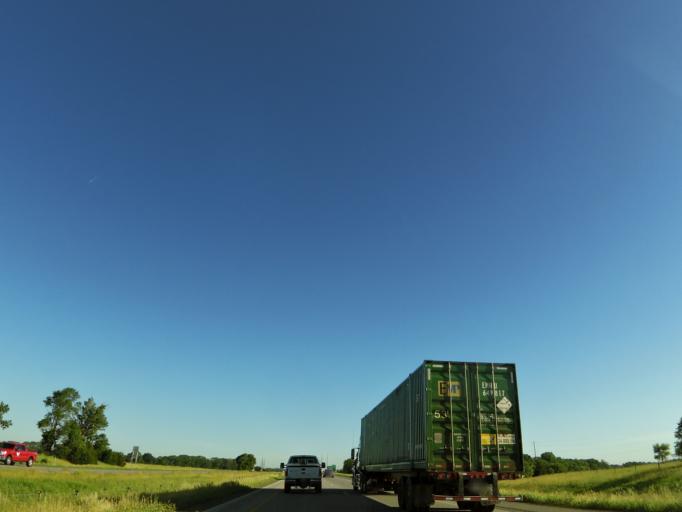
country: US
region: Minnesota
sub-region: Stearns County
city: Saint Augusta
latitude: 45.4565
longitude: -94.1247
